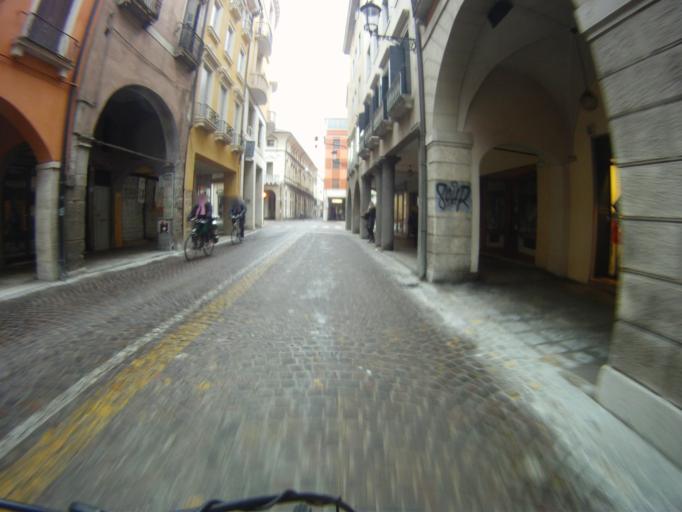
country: IT
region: Veneto
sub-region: Provincia di Padova
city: Padova
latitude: 45.4096
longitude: 11.8734
